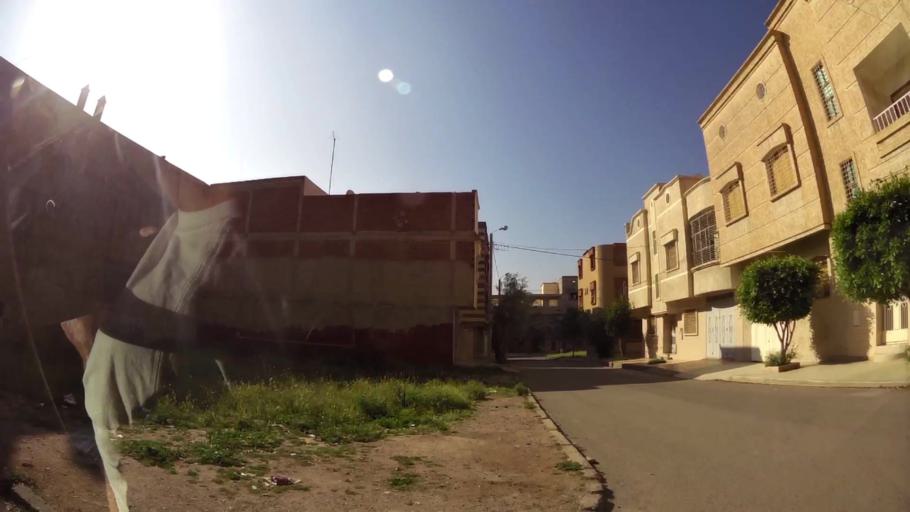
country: MA
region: Oriental
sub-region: Oujda-Angad
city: Oujda
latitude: 34.6755
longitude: -1.9354
